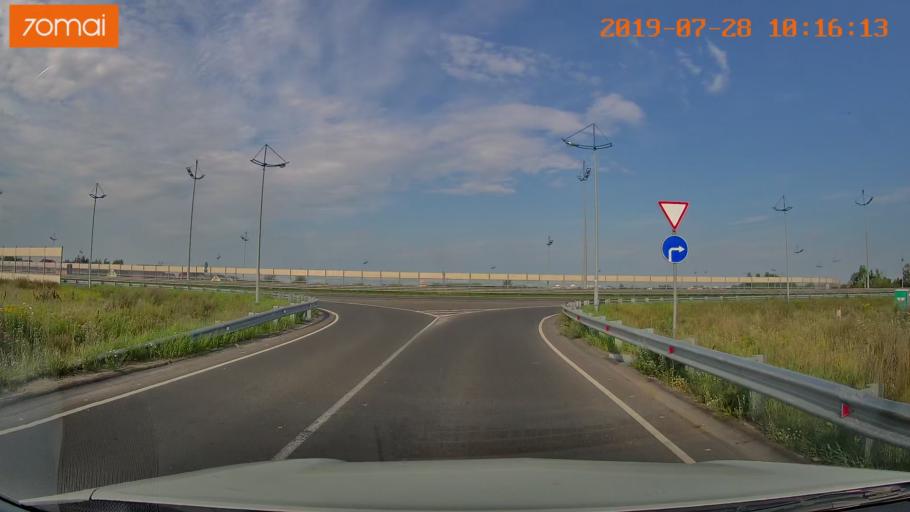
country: RU
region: Kaliningrad
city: Bol'shoe Isakovo
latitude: 54.7255
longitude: 20.5982
